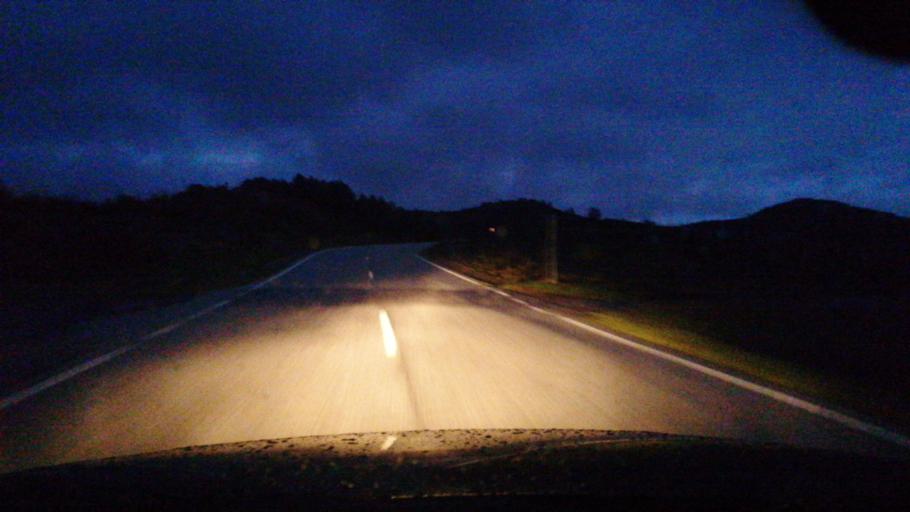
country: PT
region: Viseu
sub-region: Tabuaco
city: Tabuaco
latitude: 41.1432
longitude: -7.5360
